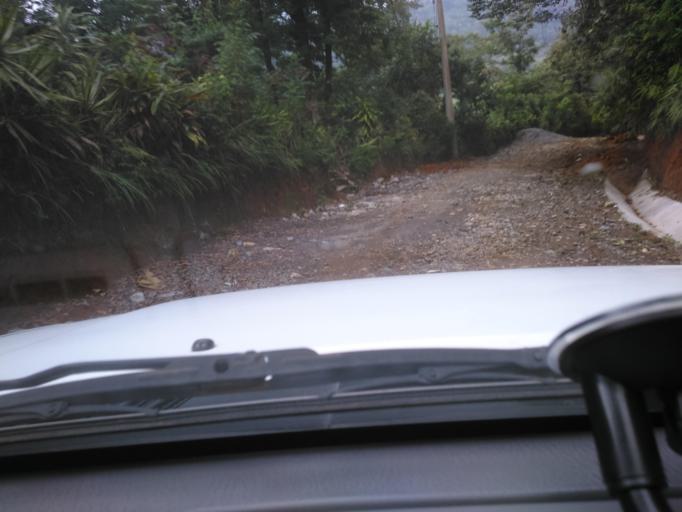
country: MX
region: Veracruz
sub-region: Mariano Escobedo
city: Chicola
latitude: 18.9129
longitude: -97.1092
